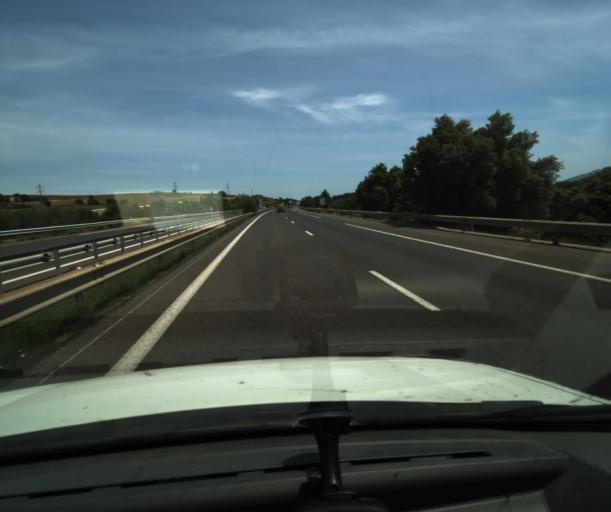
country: FR
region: Languedoc-Roussillon
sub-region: Departement des Pyrenees-Orientales
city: el Volo
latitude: 42.5319
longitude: 2.8260
